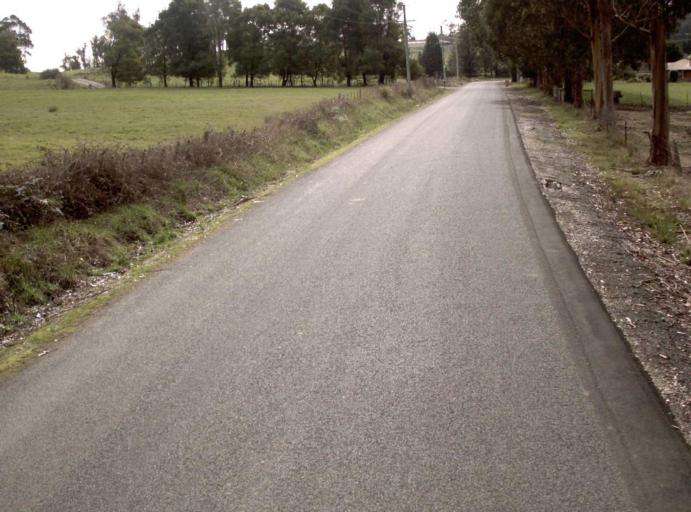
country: AU
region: Tasmania
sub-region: Launceston
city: Mayfield
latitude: -41.2682
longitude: 147.1611
